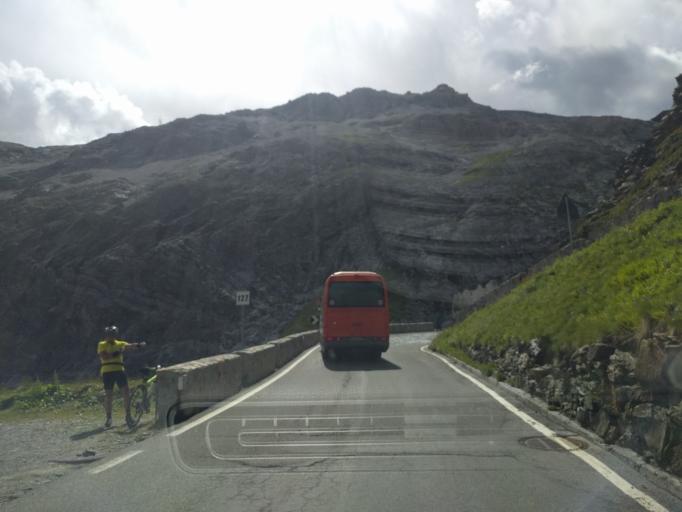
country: IT
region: Lombardy
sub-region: Provincia di Sondrio
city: Sant'Antonio
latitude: 46.5307
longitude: 10.4596
